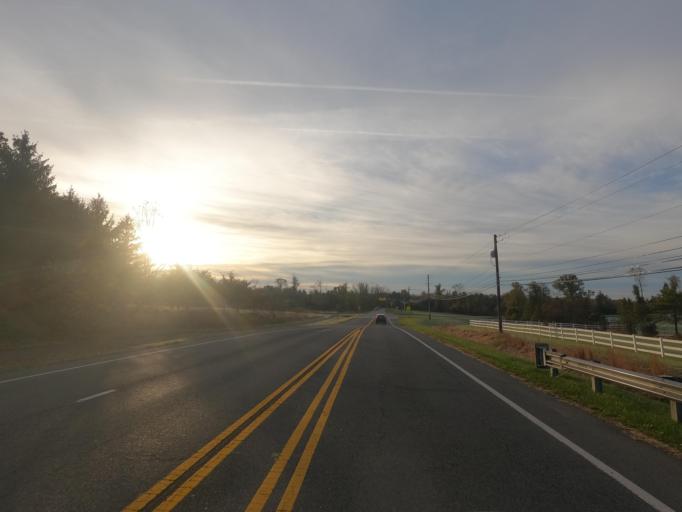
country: US
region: Maryland
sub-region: Montgomery County
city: Ashton-Sandy Spring
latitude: 39.1373
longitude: -77.0327
